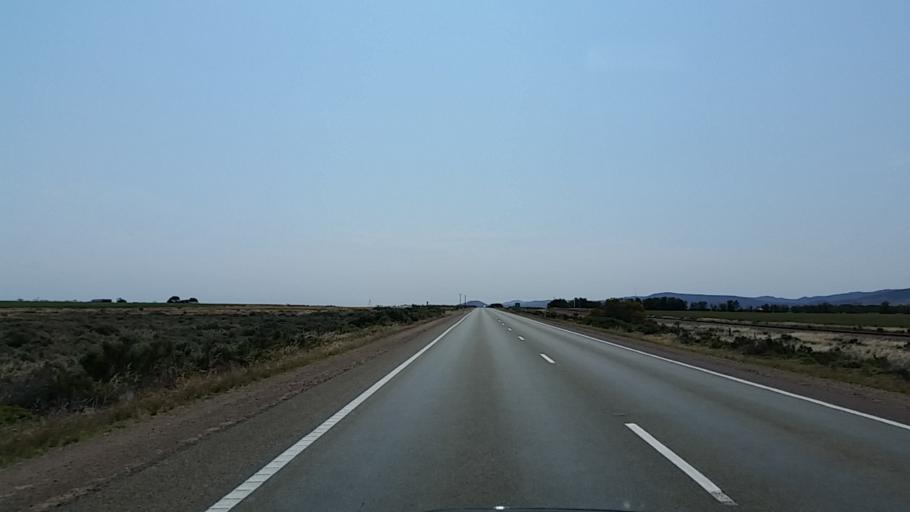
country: AU
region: South Australia
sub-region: Port Pirie City and Dists
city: Port Pirie
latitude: -32.9621
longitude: 137.9825
